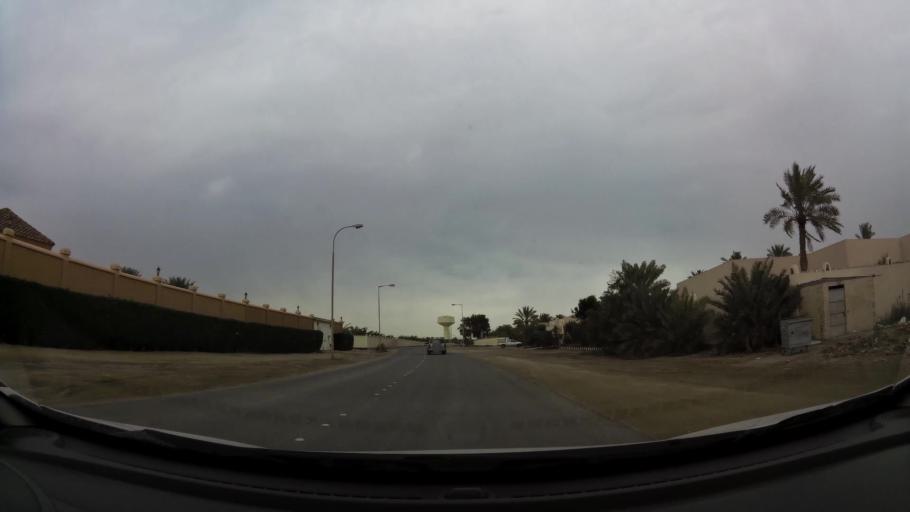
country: BH
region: Central Governorate
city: Madinat Hamad
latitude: 26.1366
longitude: 50.4634
